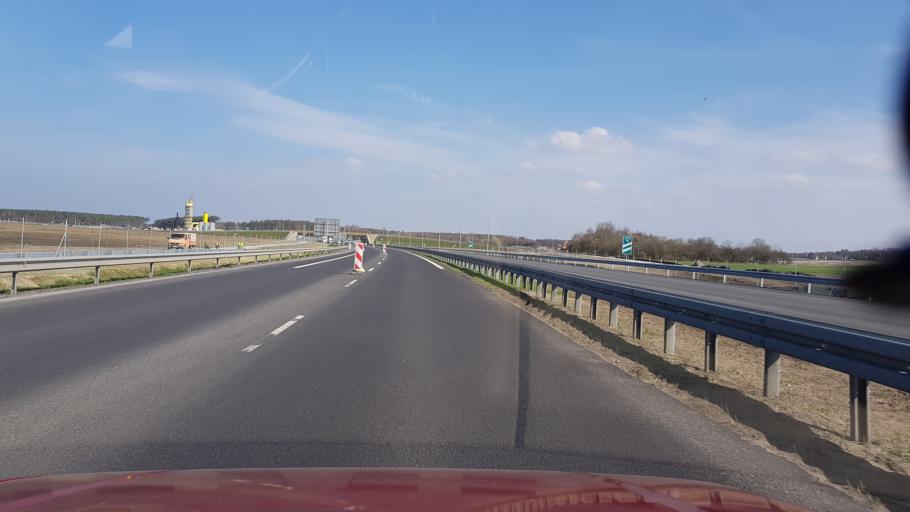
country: PL
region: West Pomeranian Voivodeship
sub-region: Powiat goleniowski
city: Goleniow
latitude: 53.5887
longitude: 14.8577
